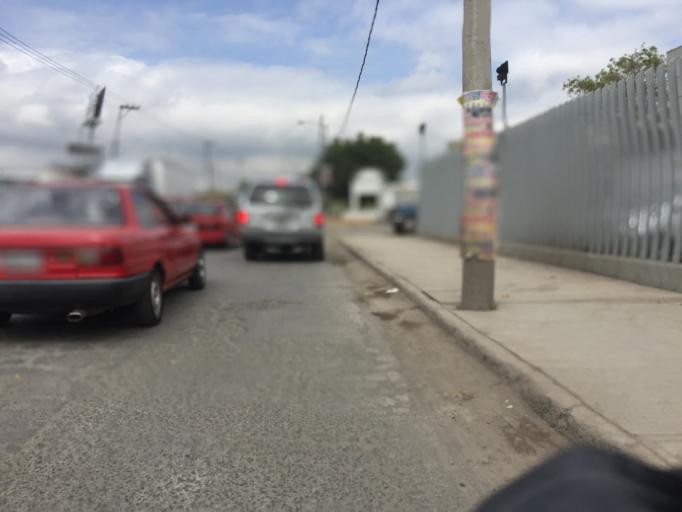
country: MX
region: Mexico
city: Cuautitlan
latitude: 19.6692
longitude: -99.1981
